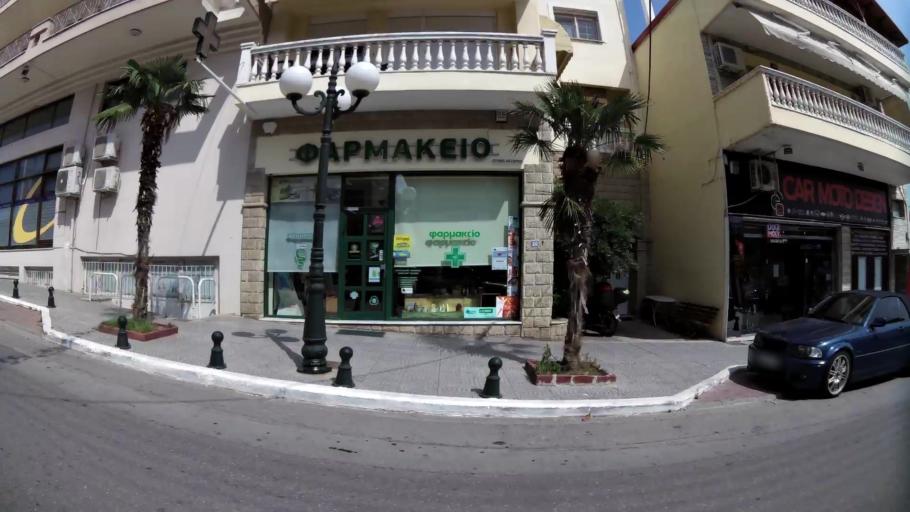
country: GR
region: Central Macedonia
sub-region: Nomos Thessalonikis
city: Efkarpia
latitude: 40.6867
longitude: 22.9538
